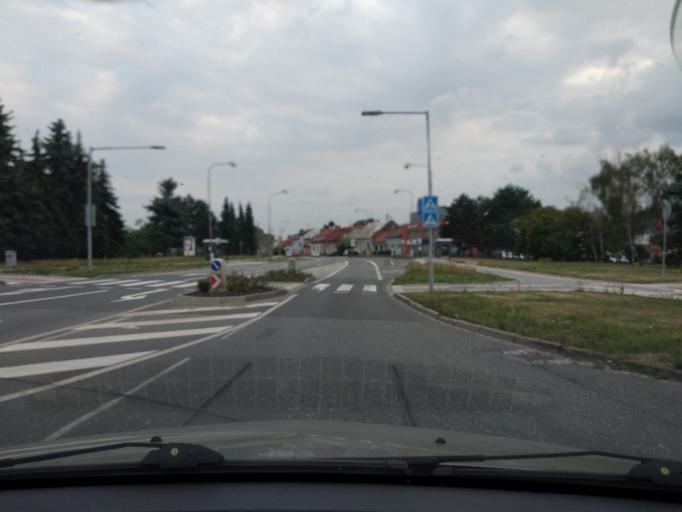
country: CZ
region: Olomoucky
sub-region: Okres Olomouc
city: Olomouc
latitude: 49.5775
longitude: 17.2579
